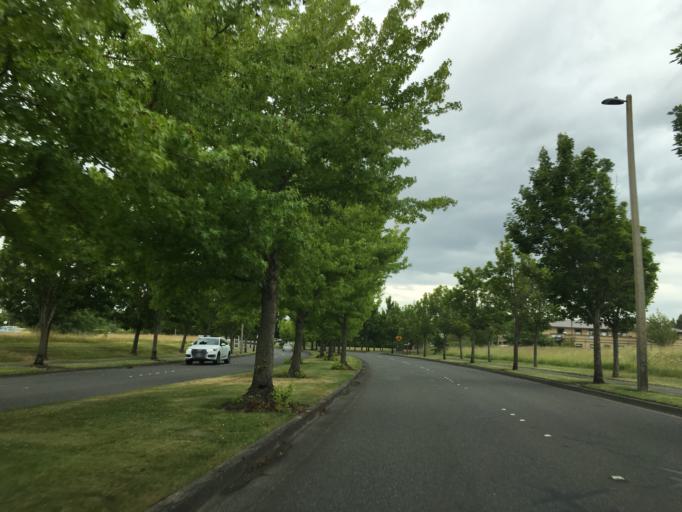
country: US
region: Washington
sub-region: Whatcom County
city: Bellingham
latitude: 48.8039
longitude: -122.4955
